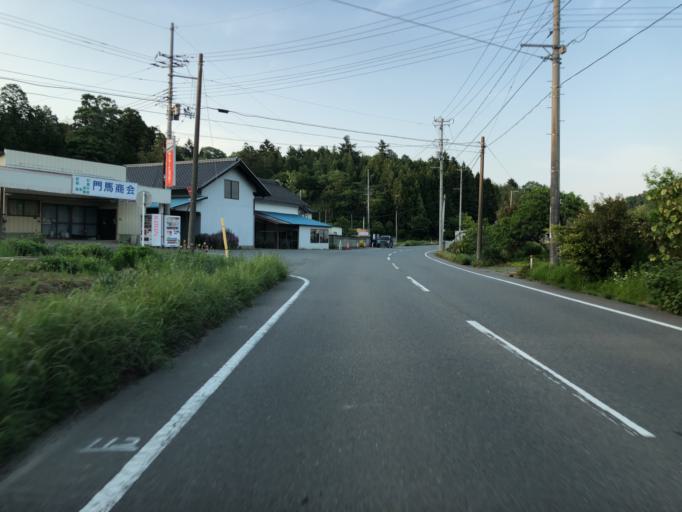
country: JP
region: Fukushima
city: Iwaki
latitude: 37.2263
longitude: 140.9748
